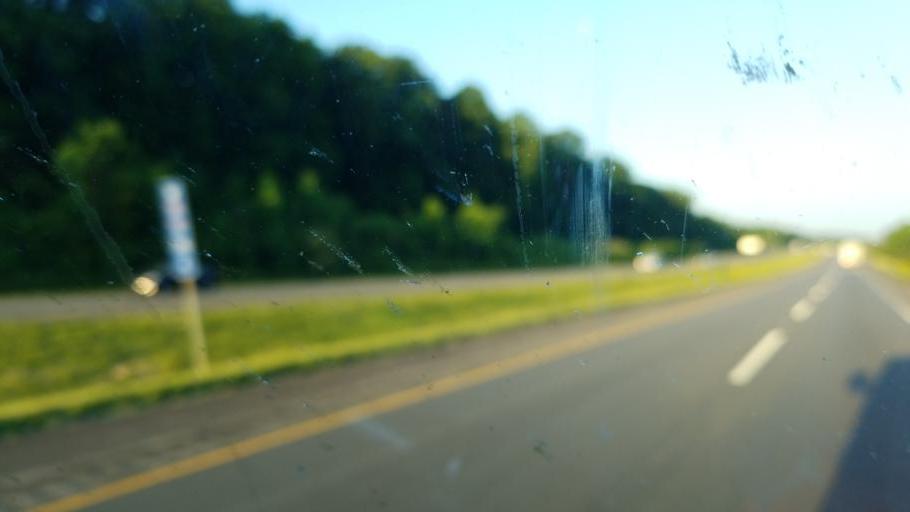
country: US
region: Indiana
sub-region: LaPorte County
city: Westville
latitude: 41.5819
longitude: -86.9461
